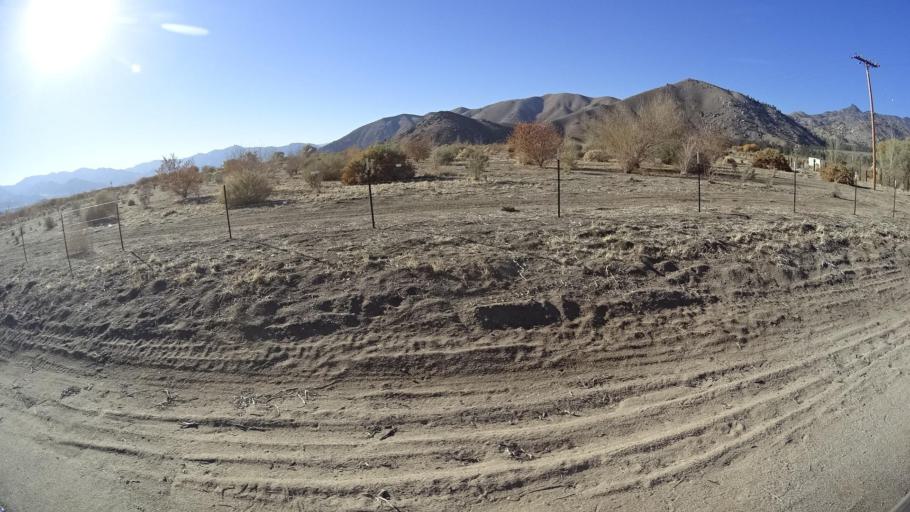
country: US
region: California
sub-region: Kern County
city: Weldon
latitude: 35.6840
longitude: -118.2901
